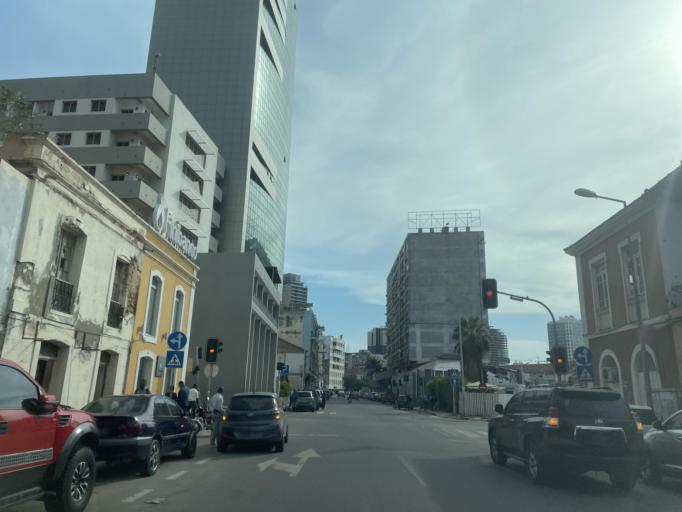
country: AO
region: Luanda
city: Luanda
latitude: -8.8107
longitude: 13.2373
